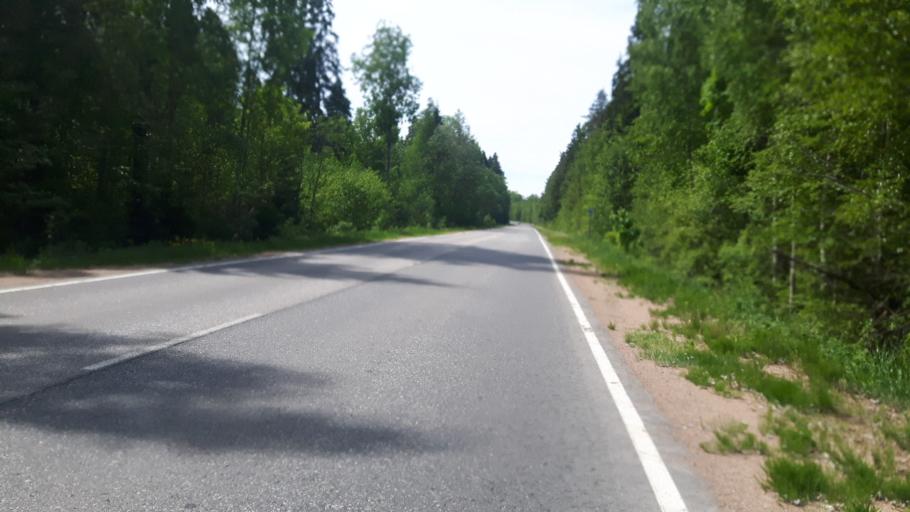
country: RU
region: Leningrad
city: Ust'-Luga
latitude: 59.6445
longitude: 28.1877
